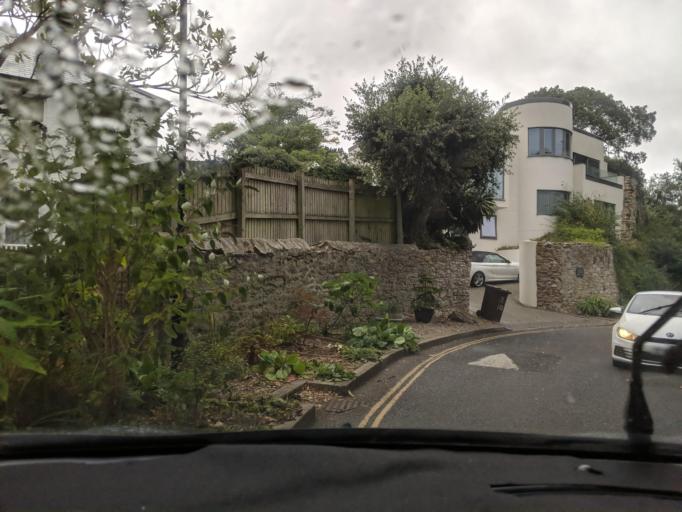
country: GB
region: England
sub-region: Plymouth
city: Plymouth
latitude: 50.3621
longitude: -4.1617
